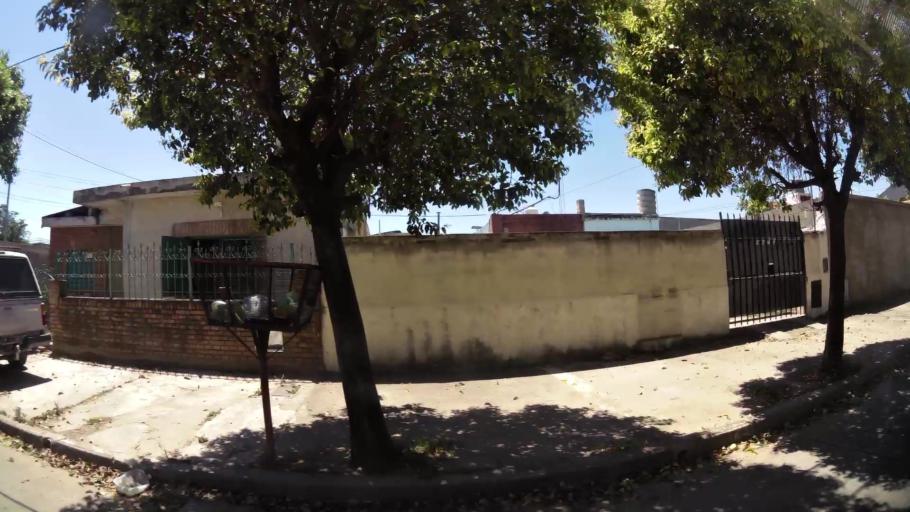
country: AR
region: Cordoba
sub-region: Departamento de Capital
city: Cordoba
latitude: -31.4406
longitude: -64.1233
